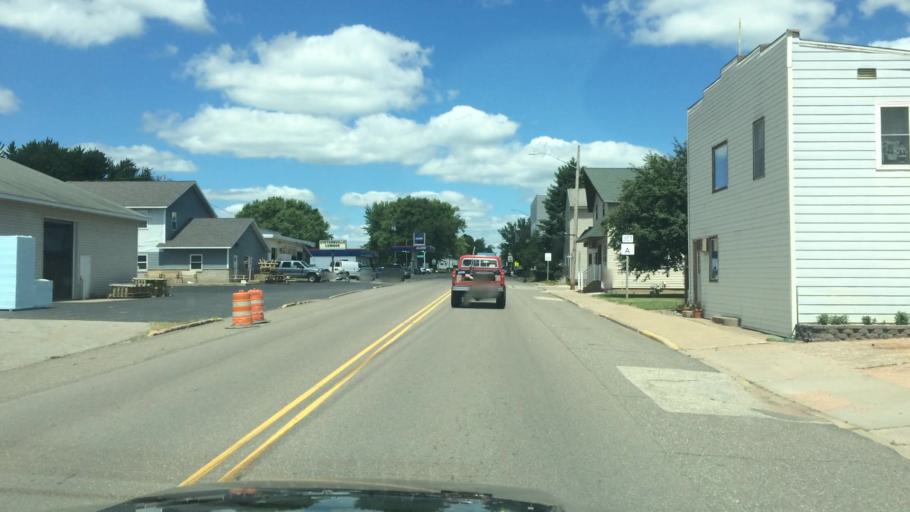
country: US
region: Wisconsin
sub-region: Taylor County
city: Medford
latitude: 45.0751
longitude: -90.3148
